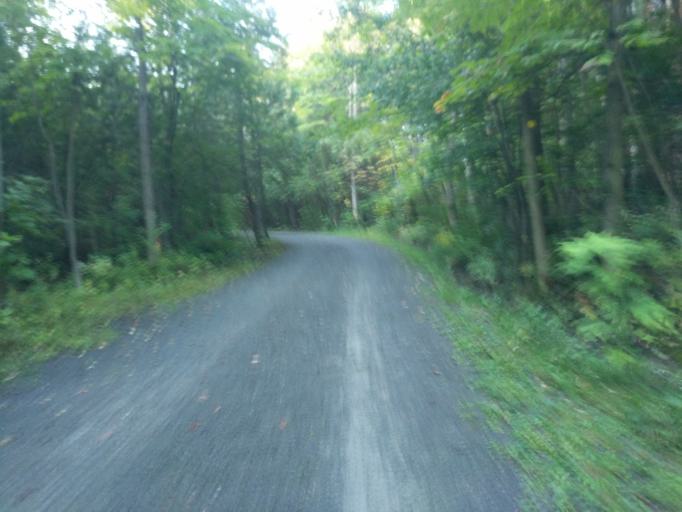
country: CA
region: Ontario
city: Bells Corners
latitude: 45.3272
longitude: -75.8604
